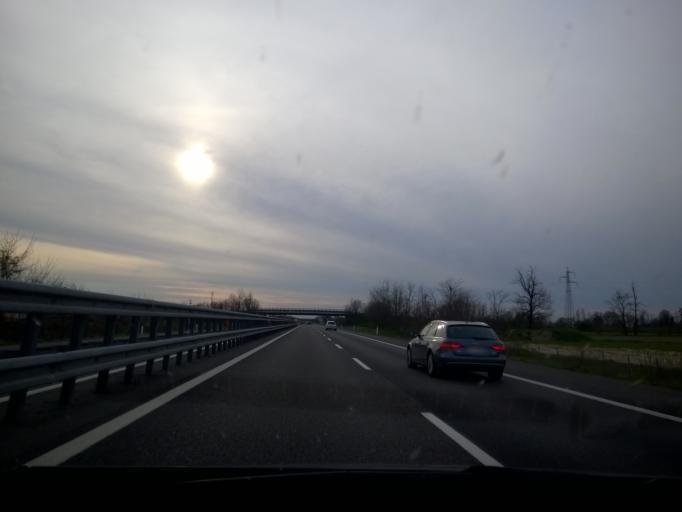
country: IT
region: Emilia-Romagna
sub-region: Provincia di Piacenza
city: San Nicolo
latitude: 45.0626
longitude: 9.6267
